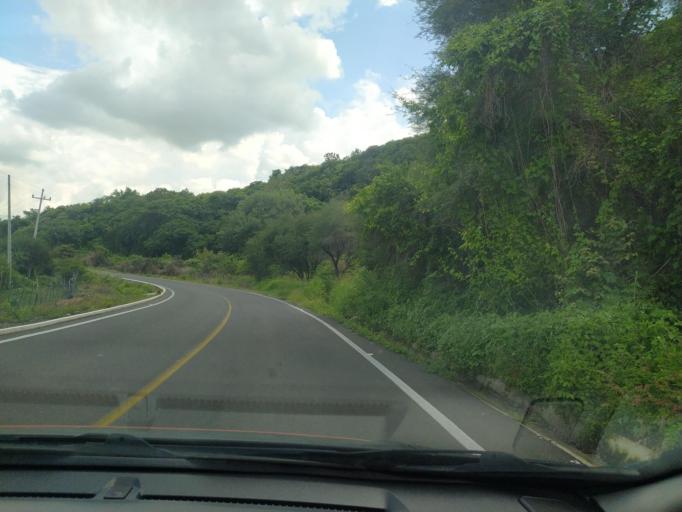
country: MX
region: Jalisco
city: Villa Corona
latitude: 20.3882
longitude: -103.6741
